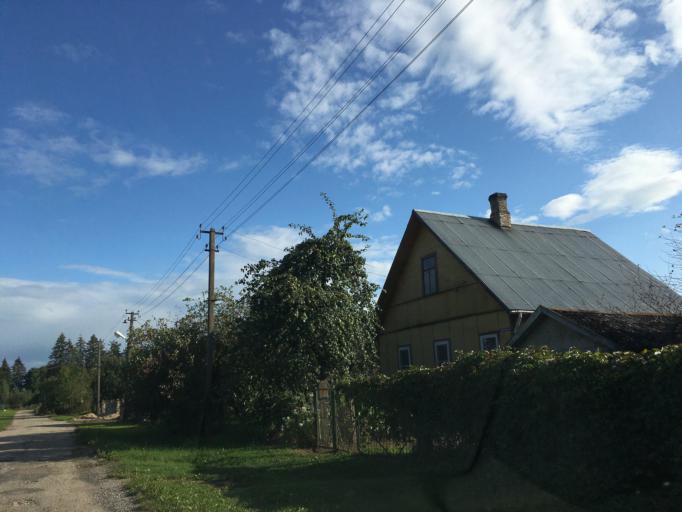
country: RU
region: Pskov
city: Izborsk
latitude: 57.7707
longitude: 27.9734
